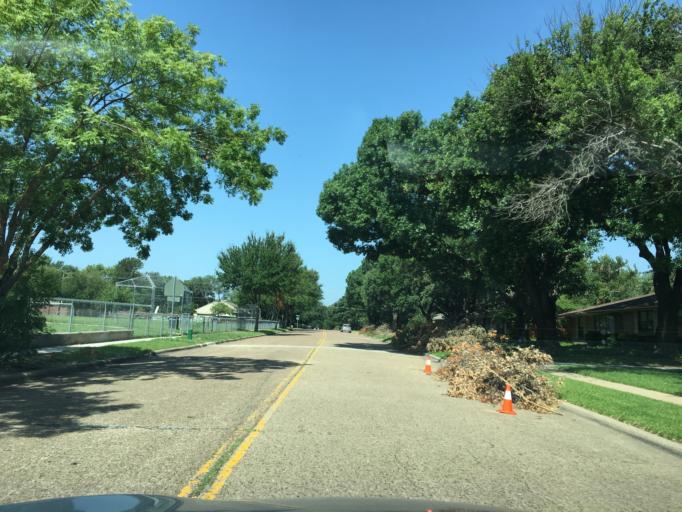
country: US
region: Texas
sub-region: Dallas County
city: University Park
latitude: 32.9032
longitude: -96.7830
